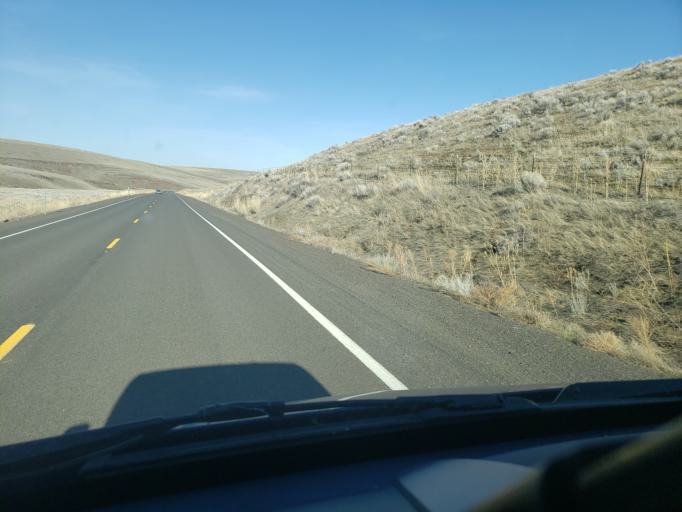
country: US
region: Oregon
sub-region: Umatilla County
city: Pilot Rock
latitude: 45.4618
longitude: -118.9297
